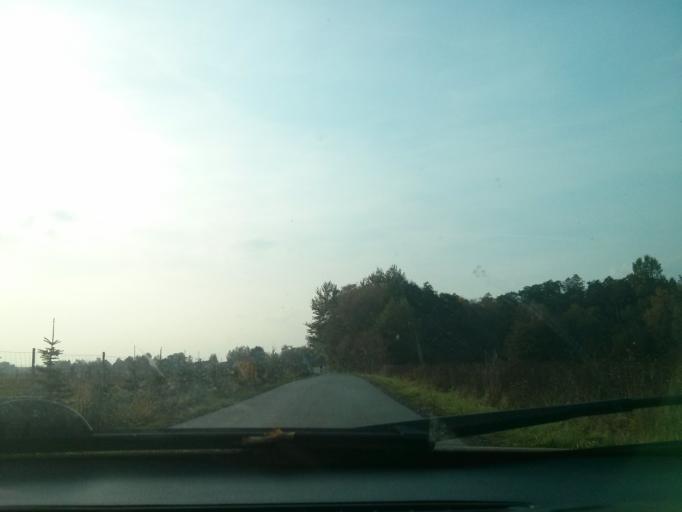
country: PL
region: Masovian Voivodeship
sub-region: Powiat piaseczynski
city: Konstancin-Jeziorna
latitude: 52.1225
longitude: 21.1573
